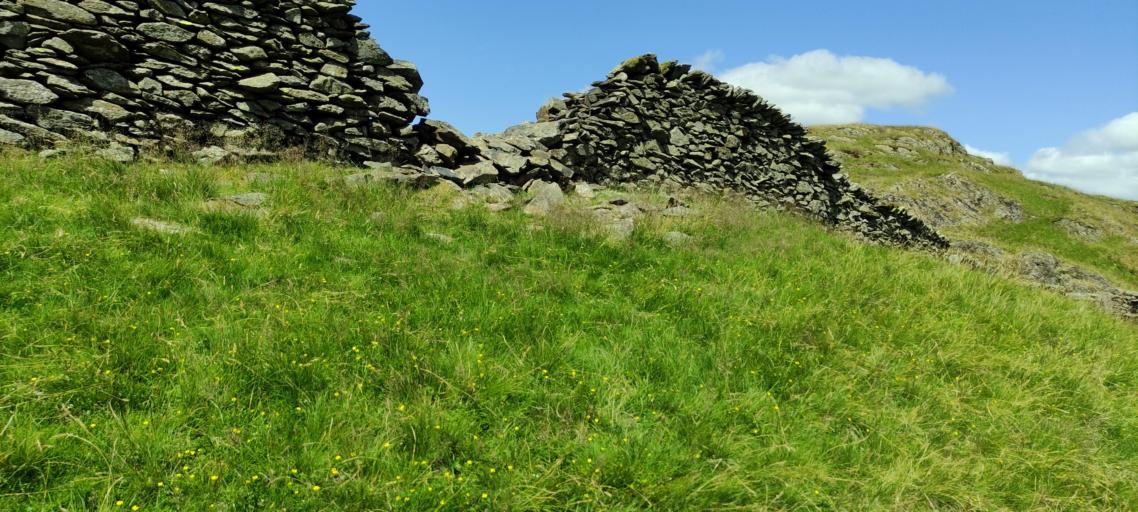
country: GB
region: England
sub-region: Cumbria
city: Ambleside
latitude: 54.4628
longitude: -3.0063
